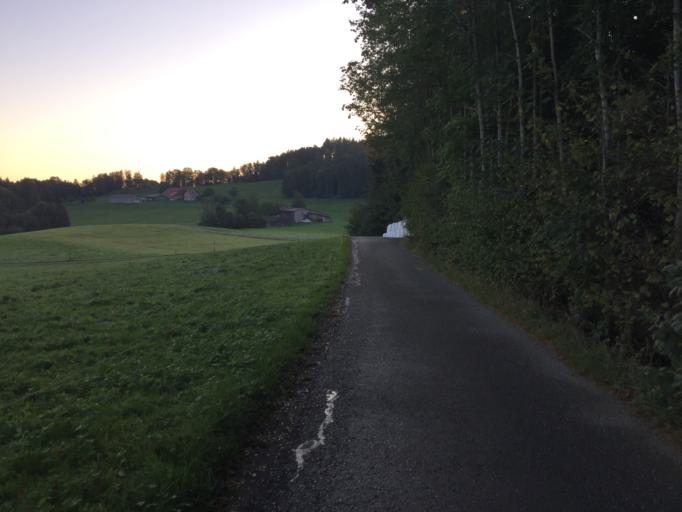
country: CH
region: Saint Gallen
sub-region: Wahlkreis Wil
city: Oberuzwil
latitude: 47.4108
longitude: 9.1410
